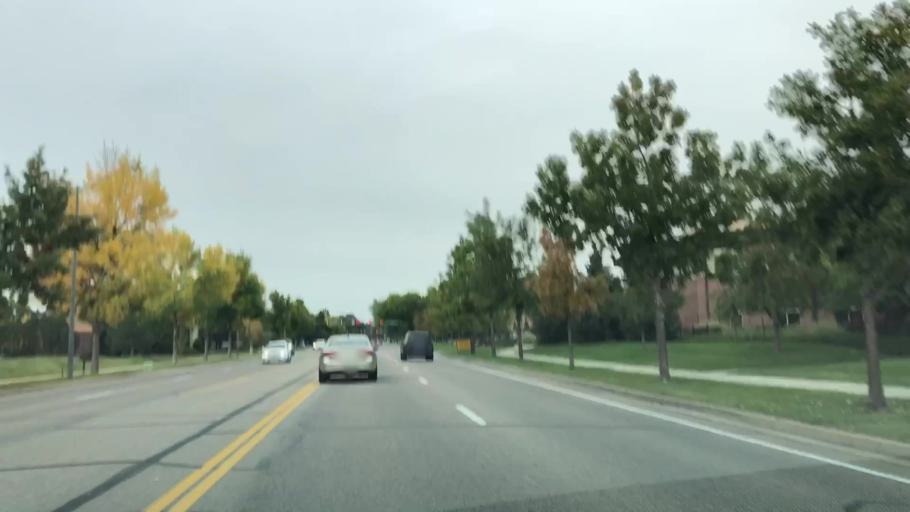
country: US
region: Colorado
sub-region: Larimer County
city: Fort Collins
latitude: 40.5191
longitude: -105.0581
